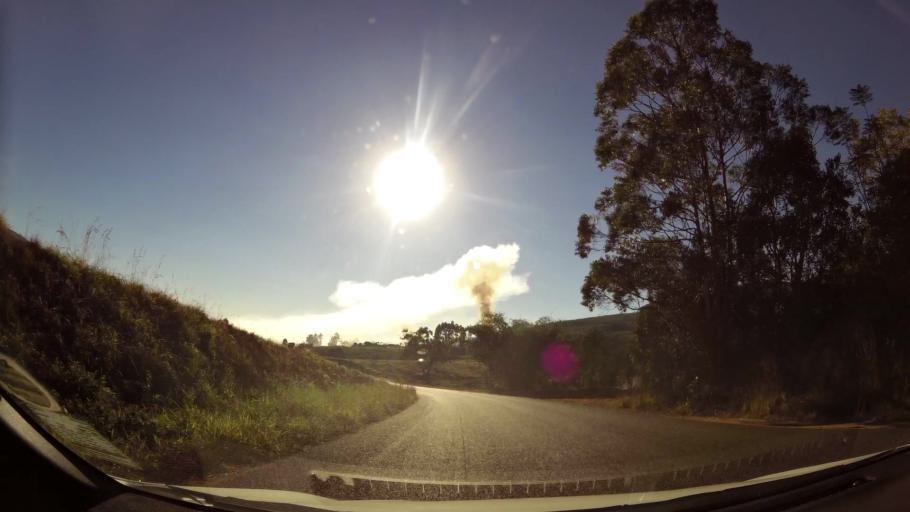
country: ZA
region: Limpopo
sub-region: Mopani District Municipality
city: Tzaneen
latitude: -23.9111
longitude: 30.0591
